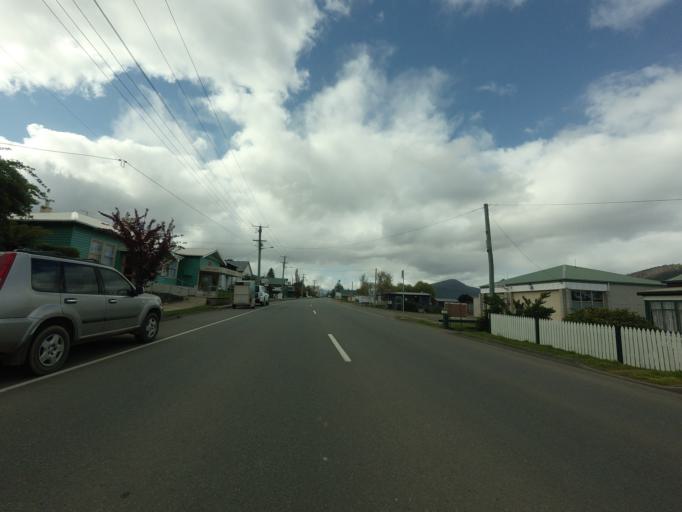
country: AU
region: Tasmania
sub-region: Huon Valley
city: Franklin
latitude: -43.0918
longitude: 147.0090
